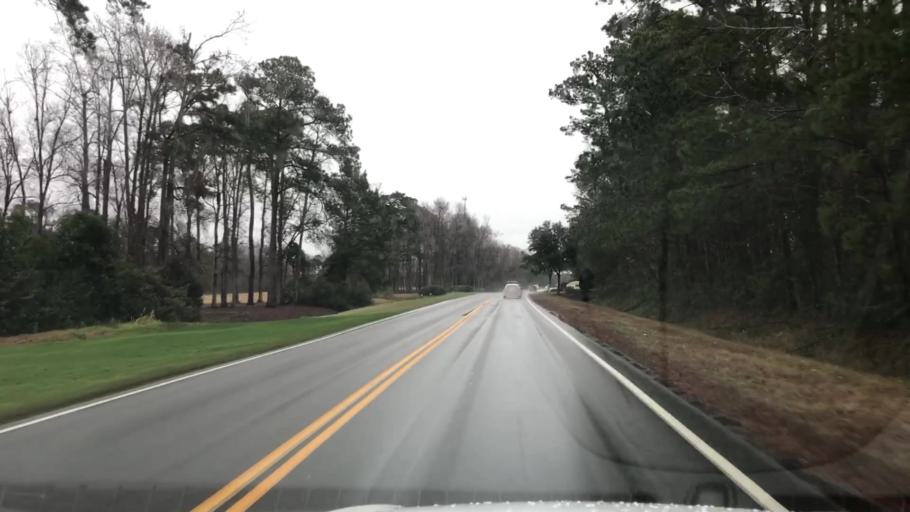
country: US
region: South Carolina
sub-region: Horry County
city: Myrtle Beach
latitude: 33.7323
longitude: -78.9057
